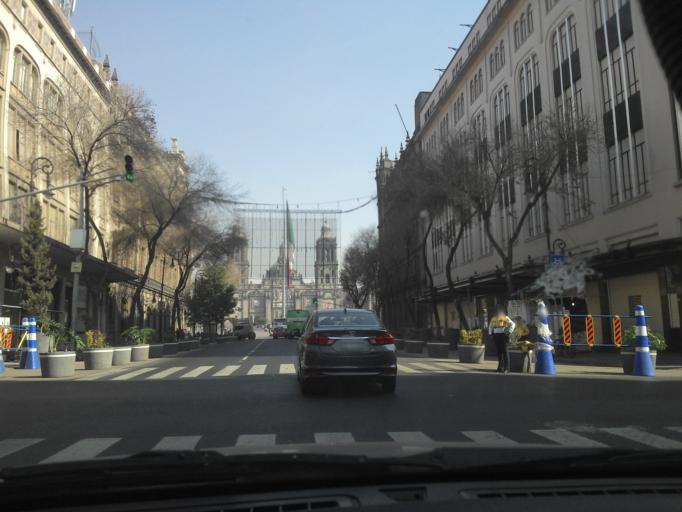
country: MX
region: Mexico City
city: Mexico City
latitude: 19.4308
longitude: -99.1336
